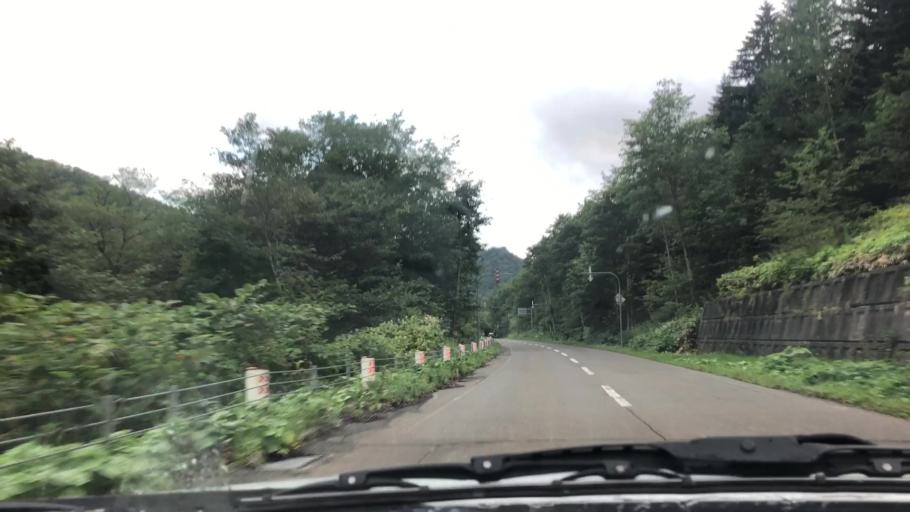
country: JP
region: Hokkaido
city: Shimo-furano
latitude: 42.9152
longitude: 142.3749
